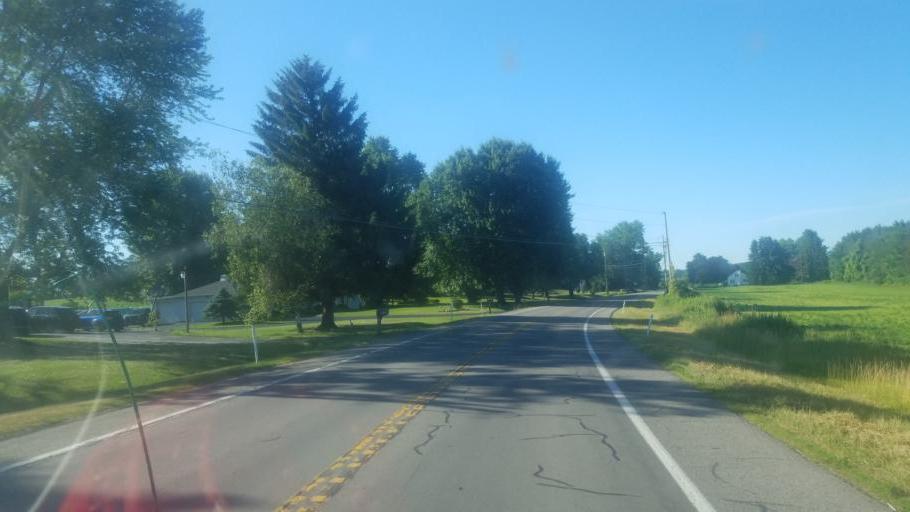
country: US
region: New York
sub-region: Ontario County
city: Phelps
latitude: 42.9959
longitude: -77.0897
